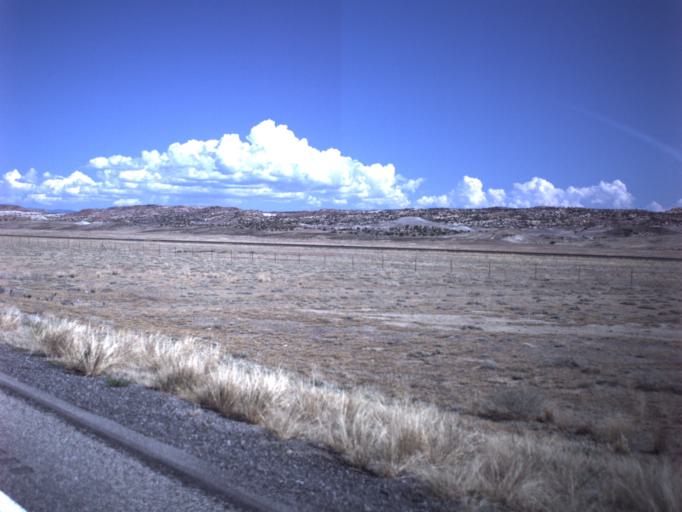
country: US
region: Utah
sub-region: Grand County
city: Moab
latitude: 38.7890
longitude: -109.7558
